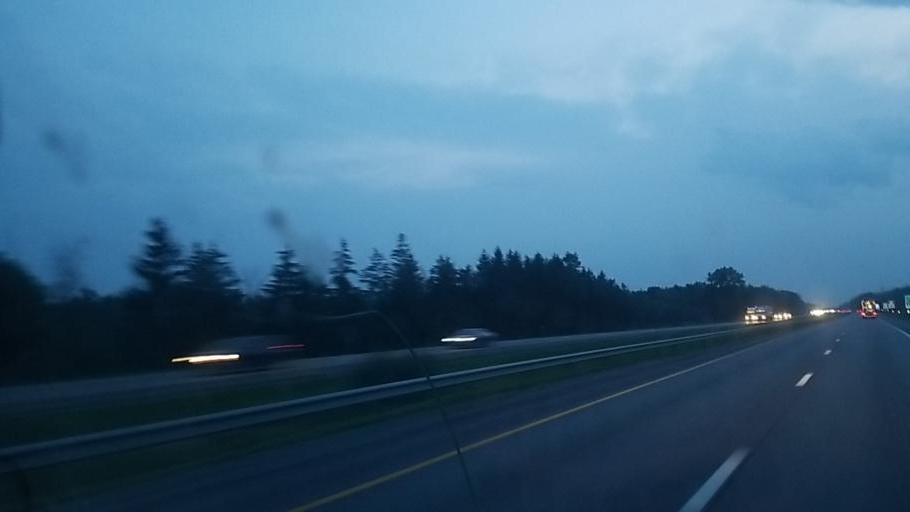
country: US
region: New York
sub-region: Onondaga County
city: Minoa
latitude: 43.0939
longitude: -75.9815
